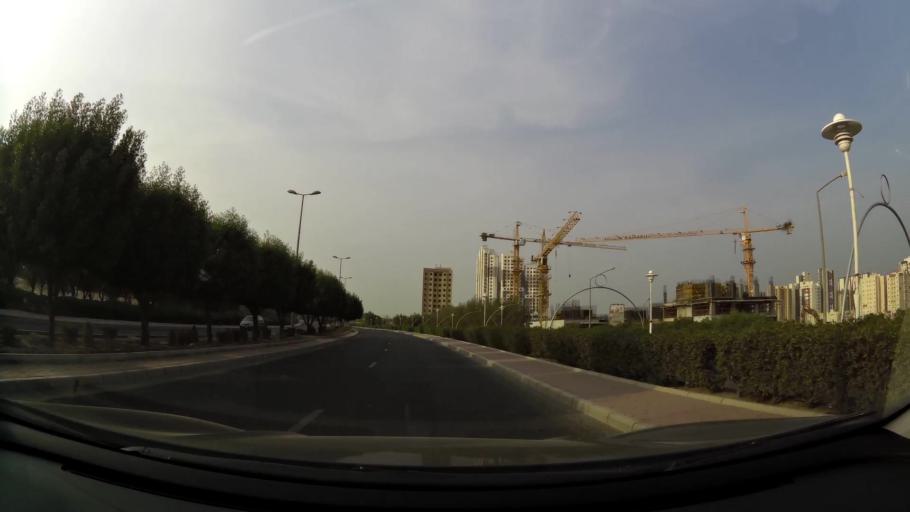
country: KW
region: Mubarak al Kabir
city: Sabah as Salim
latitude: 29.2607
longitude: 48.0787
